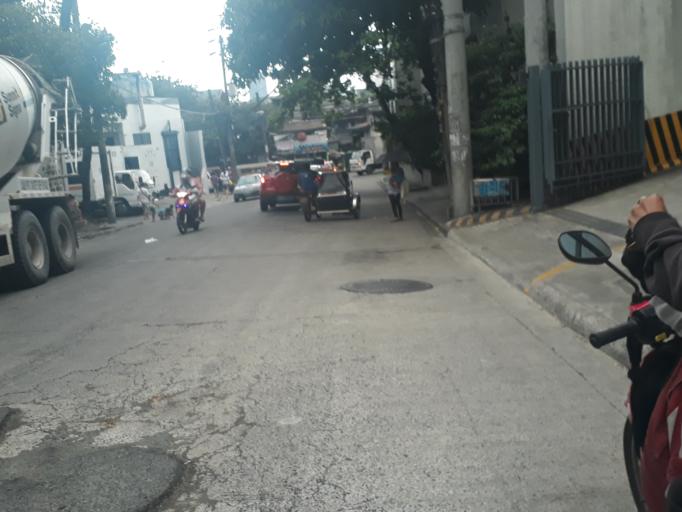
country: PH
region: Metro Manila
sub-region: Mandaluyong
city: Mandaluyong City
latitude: 14.5882
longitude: 121.0399
